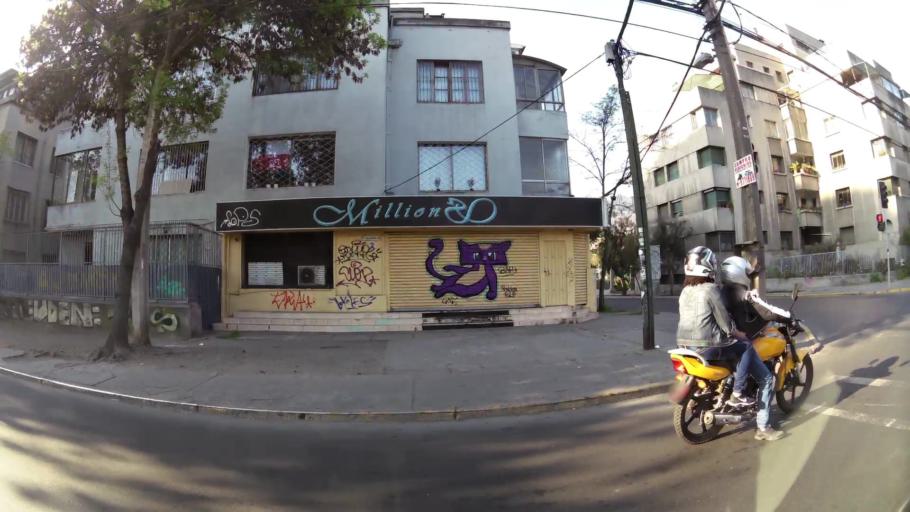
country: CL
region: Santiago Metropolitan
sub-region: Provincia de Santiago
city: Santiago
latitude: -33.4334
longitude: -70.6454
